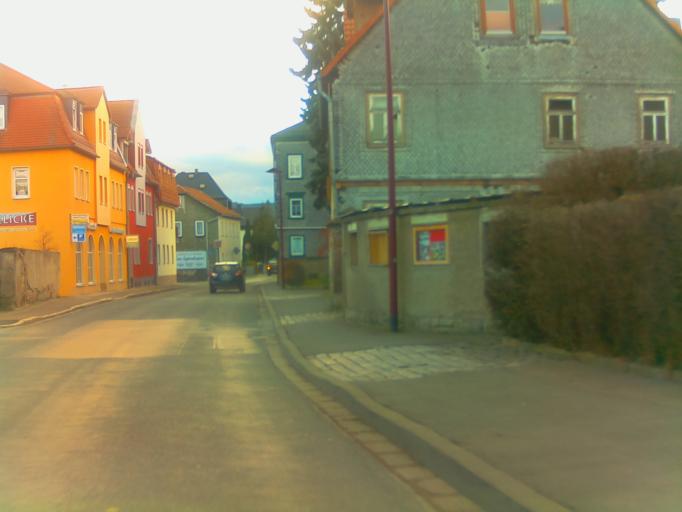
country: DE
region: Thuringia
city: Rudolstadt
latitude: 50.7059
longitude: 11.3237
